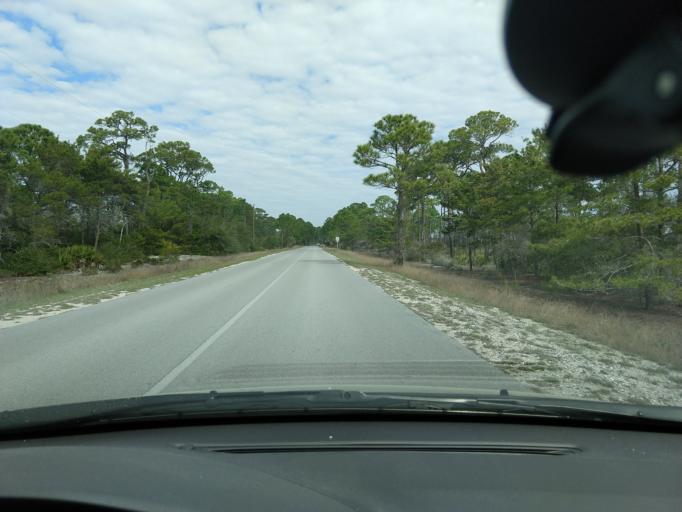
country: US
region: Florida
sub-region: Gulf County
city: Port Saint Joe
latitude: 29.7495
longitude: -85.3952
